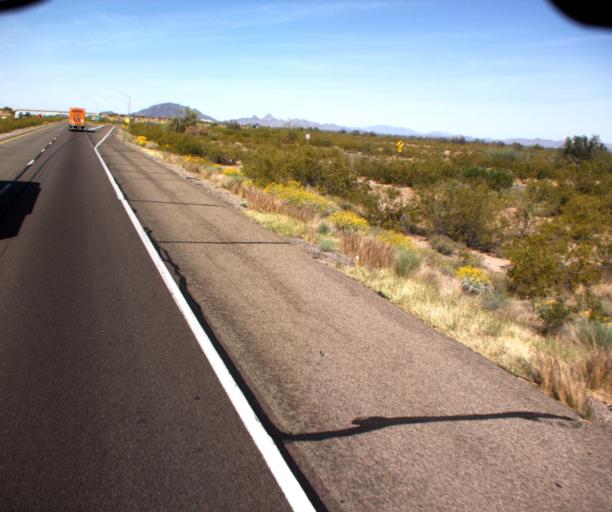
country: US
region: Arizona
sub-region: Maricopa County
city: Buckeye
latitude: 33.4961
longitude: -112.9304
